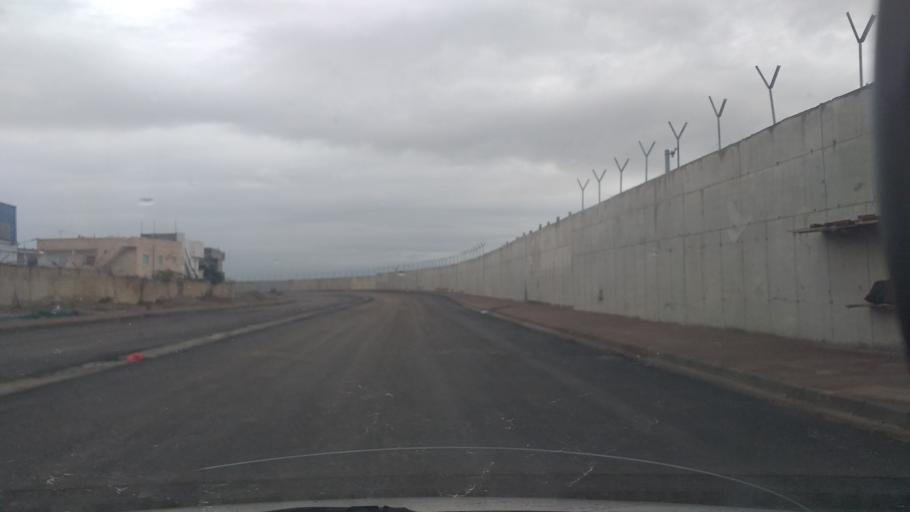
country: TN
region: Ariana
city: Ariana
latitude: 36.8651
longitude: 10.2256
